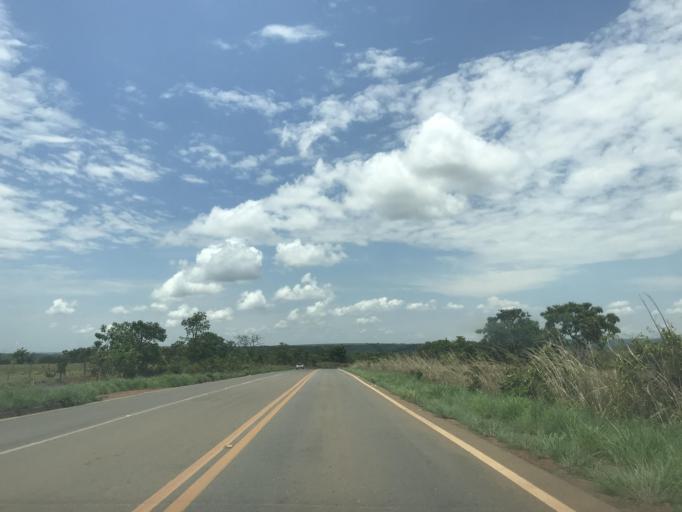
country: BR
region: Goias
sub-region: Luziania
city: Luziania
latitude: -16.3978
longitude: -48.1708
